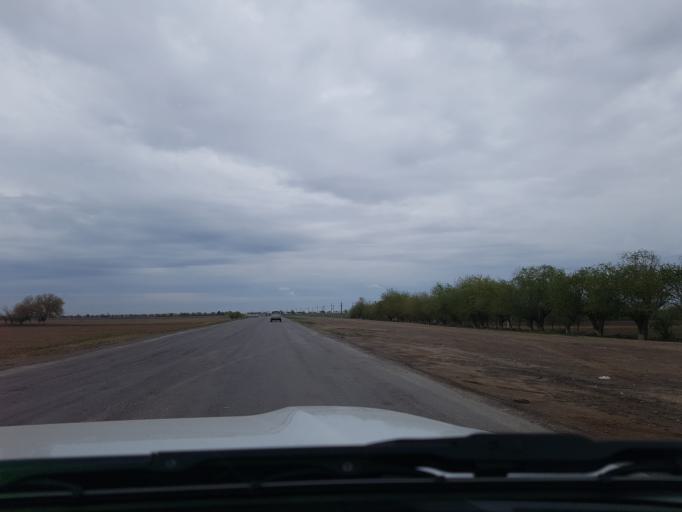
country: TM
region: Mary
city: Bayramaly
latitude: 37.6157
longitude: 62.3032
